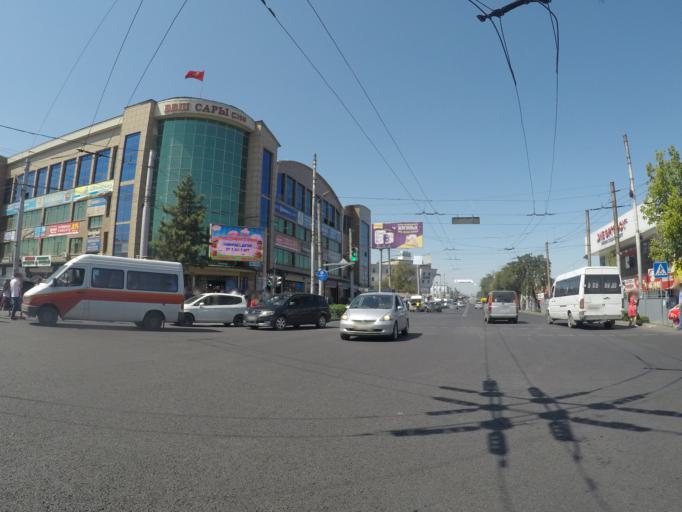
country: KG
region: Chuy
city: Bishkek
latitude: 42.8773
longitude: 74.5718
